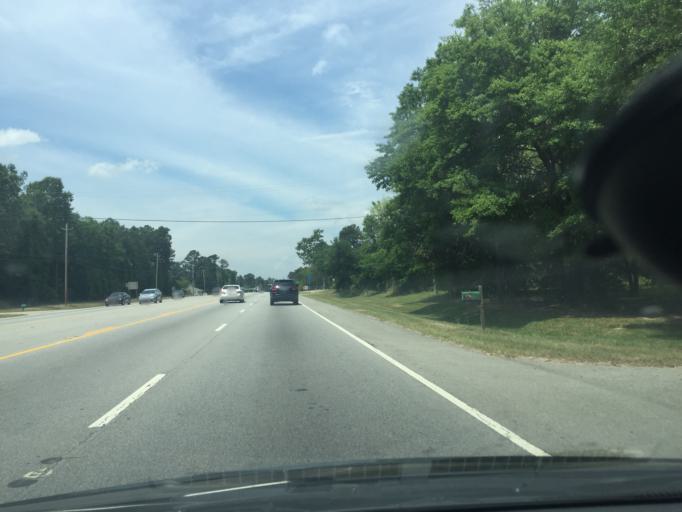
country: US
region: Georgia
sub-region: Chatham County
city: Bloomingdale
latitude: 32.1413
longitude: -81.3262
